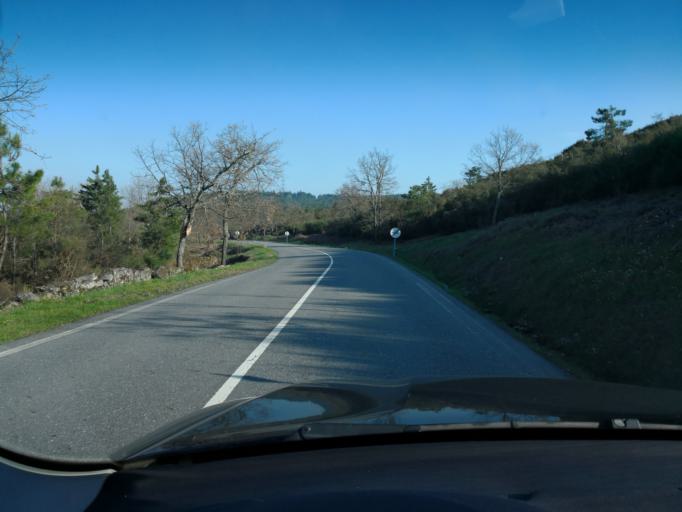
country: PT
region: Vila Real
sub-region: Sabrosa
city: Sabrosa
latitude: 41.3603
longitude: -7.6349
